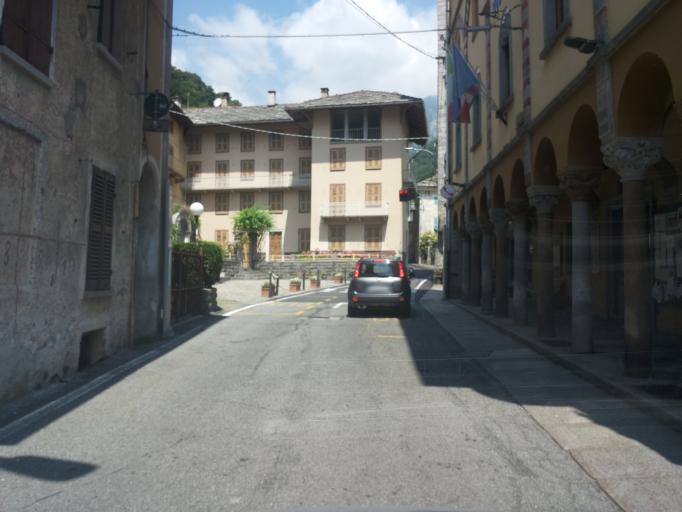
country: IT
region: Piedmont
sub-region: Provincia di Biella
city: Rosazza
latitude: 45.6760
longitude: 7.9774
